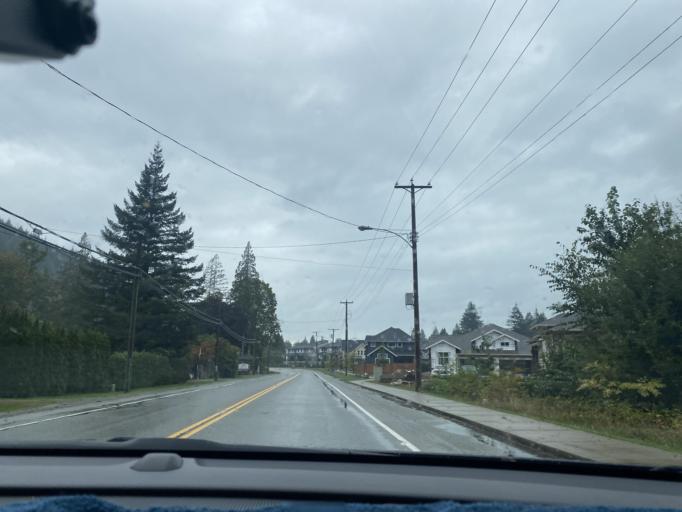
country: CA
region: British Columbia
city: Agassiz
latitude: 49.2916
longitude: -121.7803
